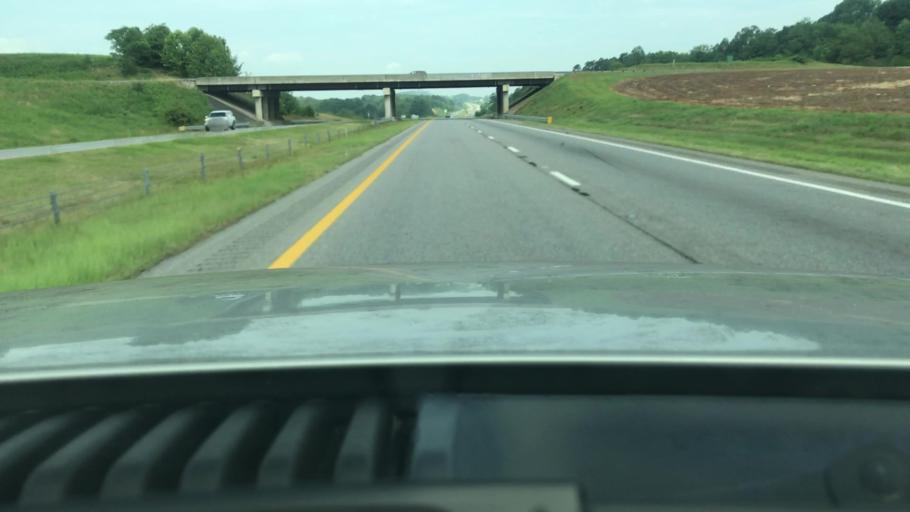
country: US
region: North Carolina
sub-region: Yadkin County
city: Jonesville
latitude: 36.1302
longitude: -80.8407
